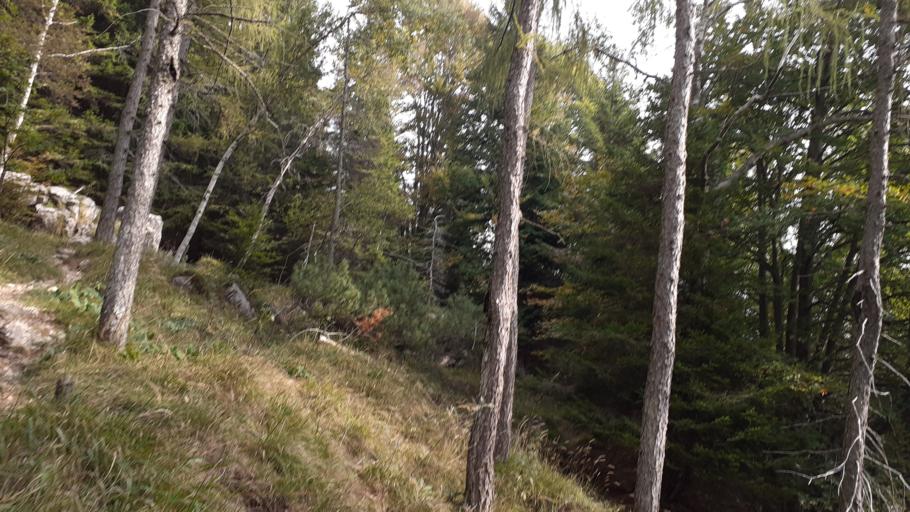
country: IT
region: Lombardy
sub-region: Provincia di Lecco
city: Ballabio
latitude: 45.9121
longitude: 9.3989
